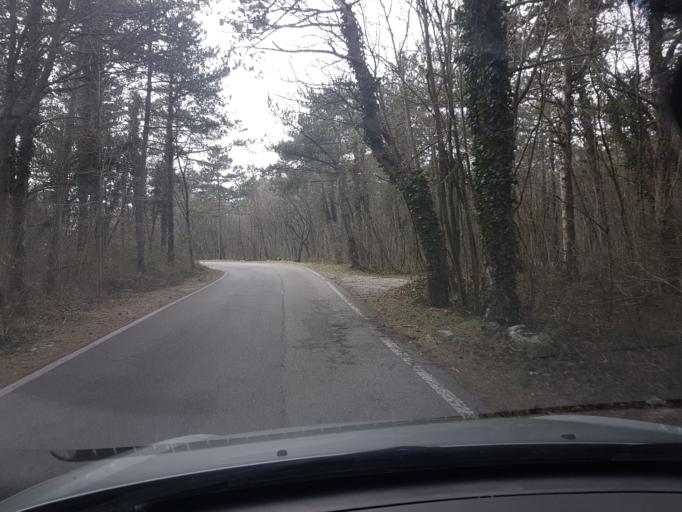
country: IT
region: Friuli Venezia Giulia
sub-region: Provincia di Trieste
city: Aurisina
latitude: 45.7641
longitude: 13.6979
